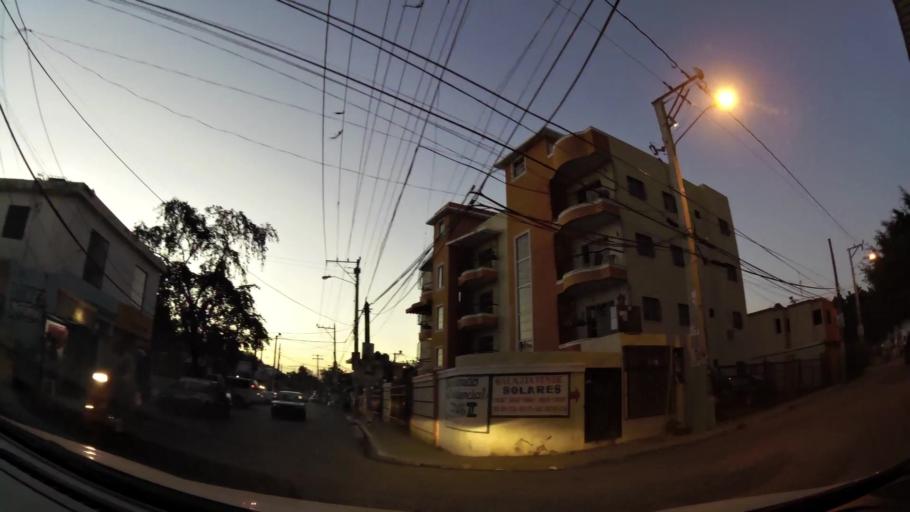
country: DO
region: Santo Domingo
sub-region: Santo Domingo
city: Santo Domingo Este
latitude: 18.5004
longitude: -69.8378
